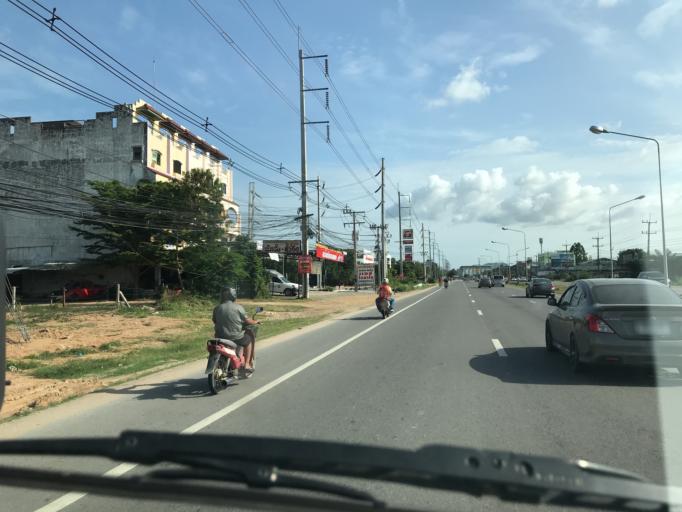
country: TH
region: Chon Buri
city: Bang Lamung
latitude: 13.0588
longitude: 100.9255
